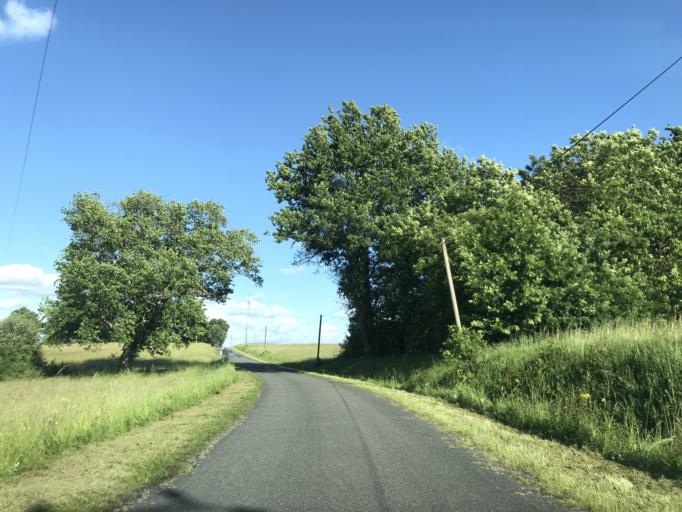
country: FR
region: Poitou-Charentes
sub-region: Departement de la Charente
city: Chalais
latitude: 45.2742
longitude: -0.0256
